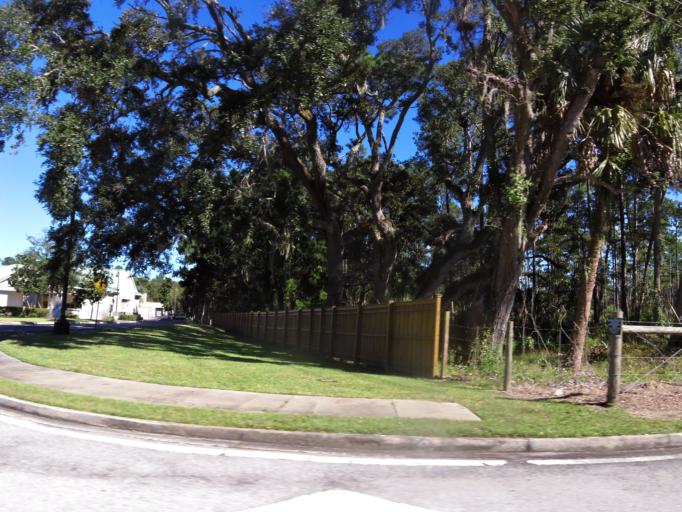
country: US
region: Florida
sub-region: Saint Johns County
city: Palm Valley
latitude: 30.1502
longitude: -81.3774
